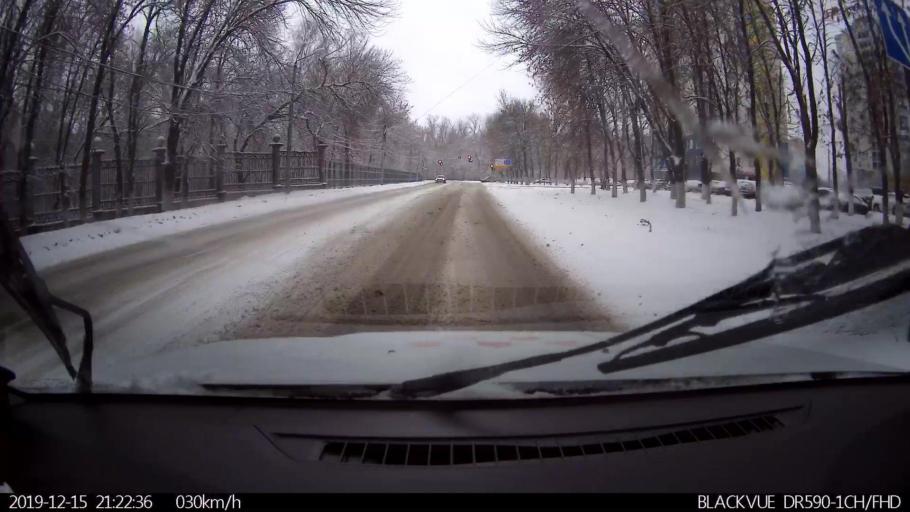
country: RU
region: Nizjnij Novgorod
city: Gorbatovka
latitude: 56.2414
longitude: 43.8491
